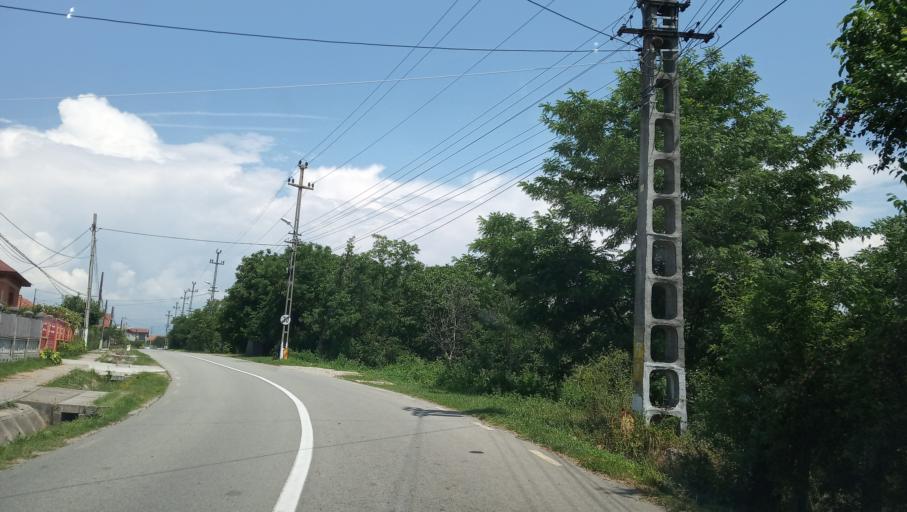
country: RO
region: Gorj
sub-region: Comuna Turcinesti
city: Turcinesti
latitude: 45.0523
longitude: 23.3472
